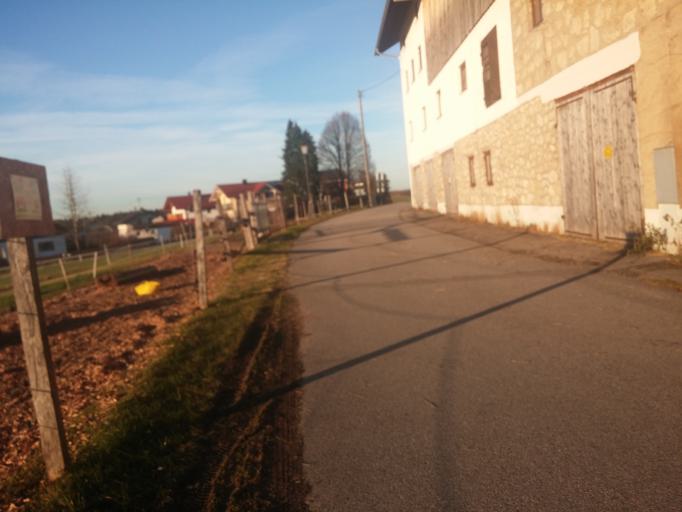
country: DE
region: Bavaria
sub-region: Upper Bavaria
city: Tuntenhausen
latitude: 47.9503
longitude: 12.0346
